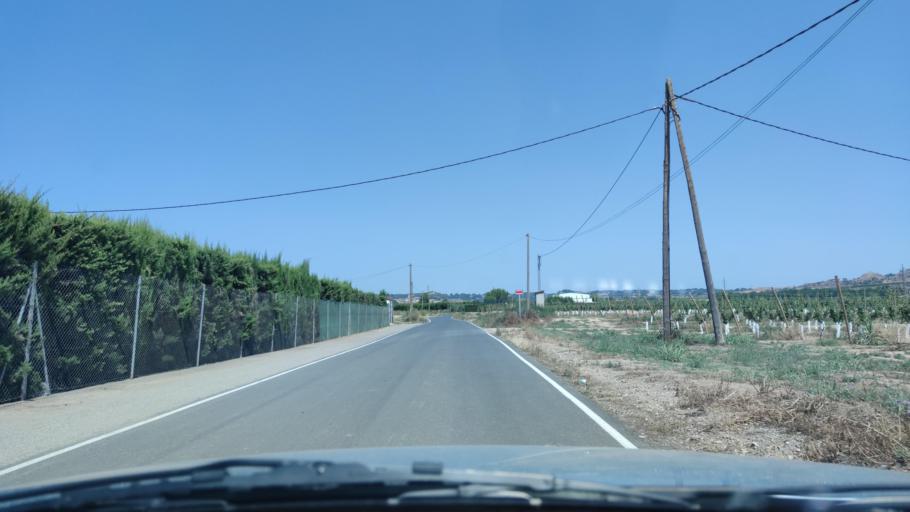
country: ES
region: Catalonia
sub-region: Provincia de Lleida
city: Alpicat
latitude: 41.6559
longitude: 0.5727
